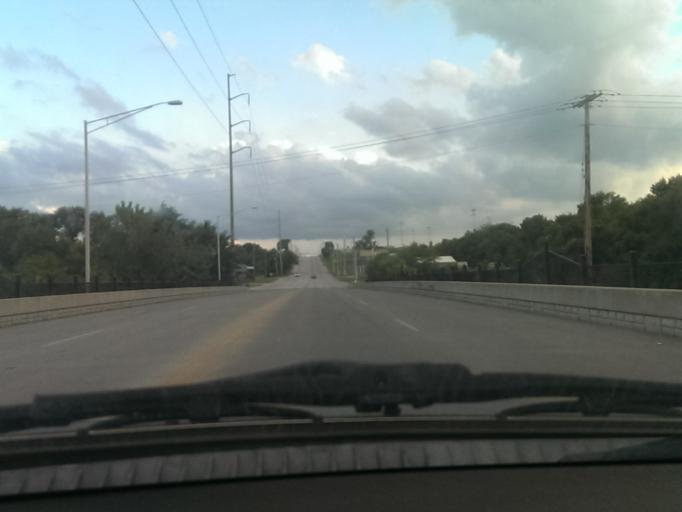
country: US
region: Kansas
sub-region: Johnson County
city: Leawood
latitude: 38.9735
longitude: -94.5766
